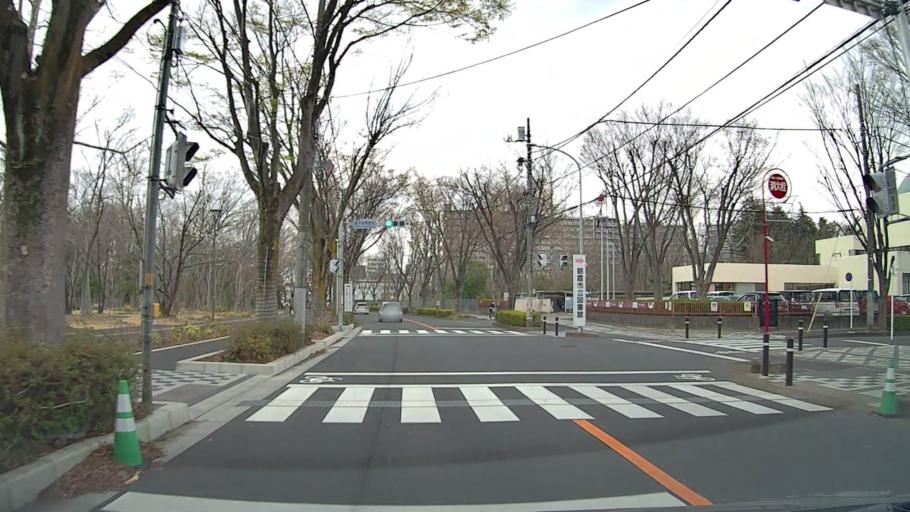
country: JP
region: Saitama
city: Asaka
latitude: 35.7932
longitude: 139.5945
